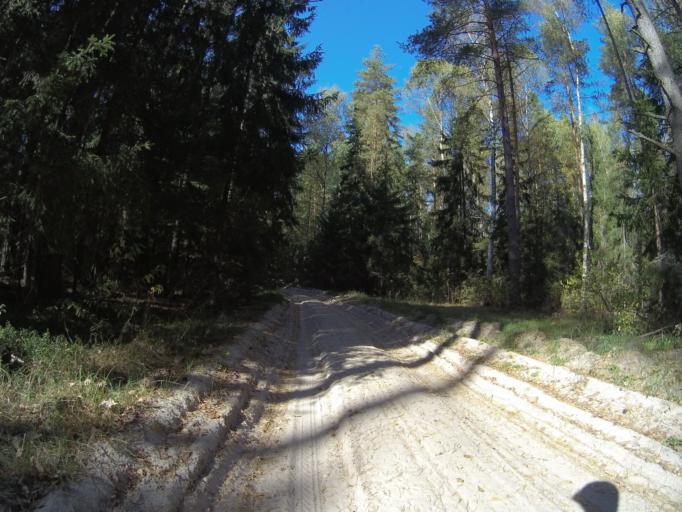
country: RU
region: Vladimir
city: Vorsha
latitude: 55.9700
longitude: 40.1536
